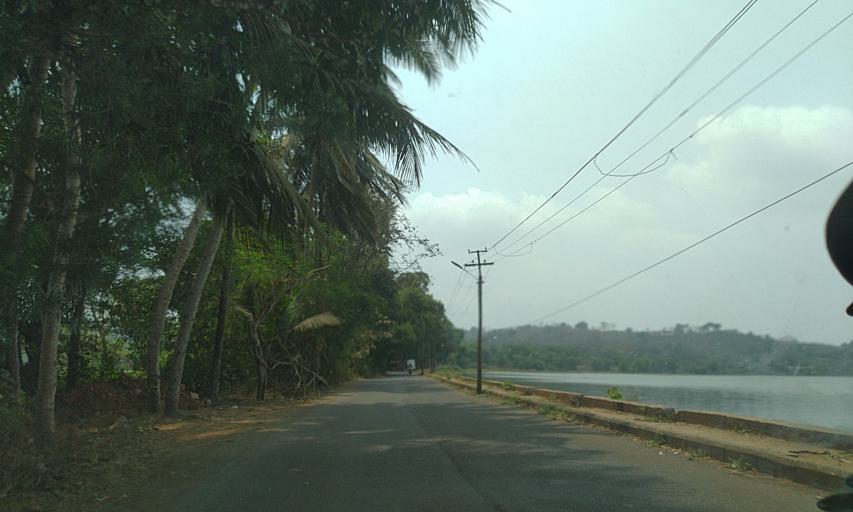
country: IN
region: Goa
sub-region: North Goa
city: Jua
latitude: 15.4861
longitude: 73.9293
